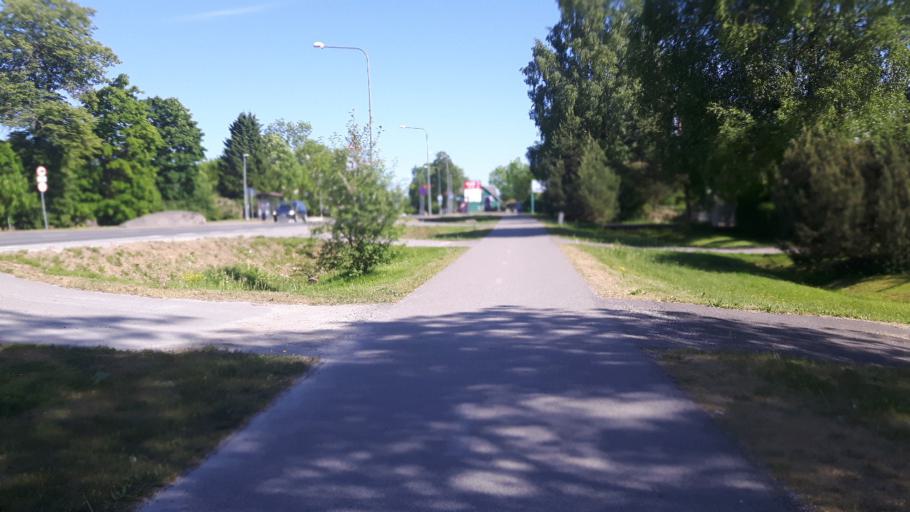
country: EE
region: Raplamaa
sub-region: Rapla vald
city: Rapla
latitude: 58.9977
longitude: 24.8091
